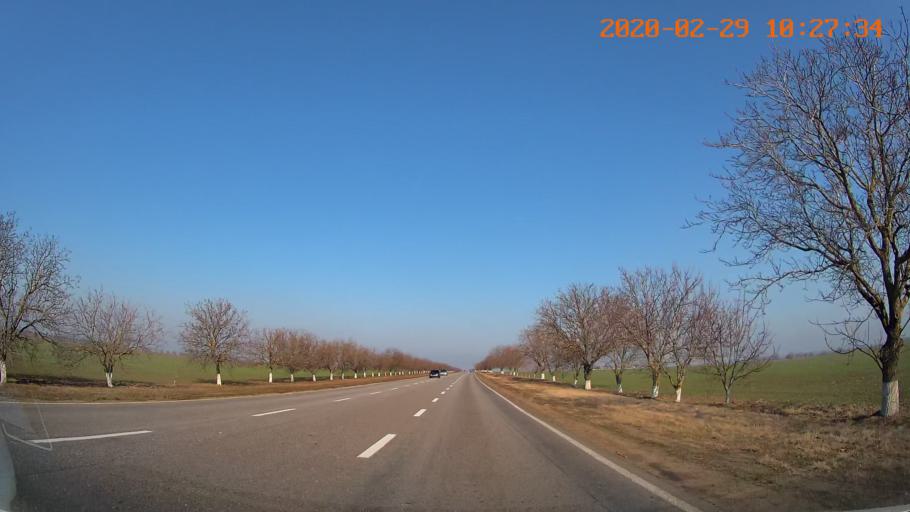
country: MD
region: Telenesti
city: Tiraspolul Nou
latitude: 46.8979
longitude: 29.5969
